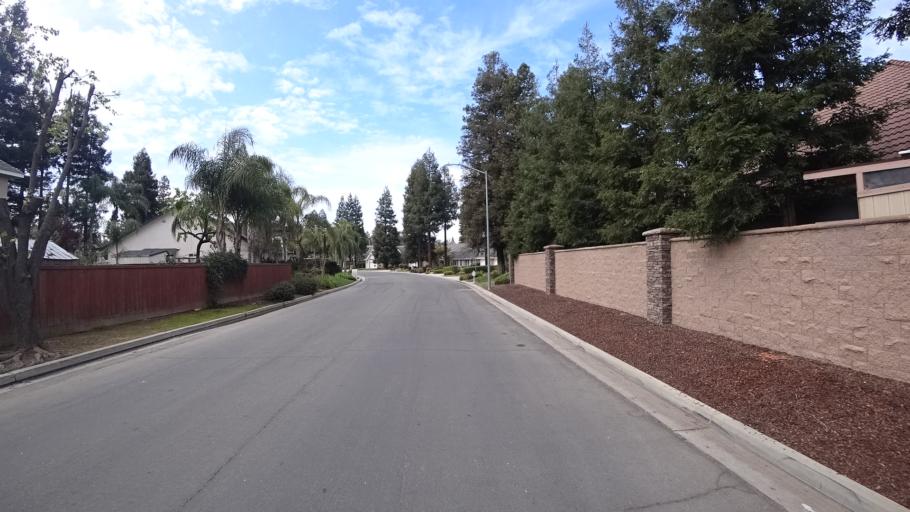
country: US
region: California
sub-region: Fresno County
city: West Park
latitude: 36.8416
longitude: -119.8802
